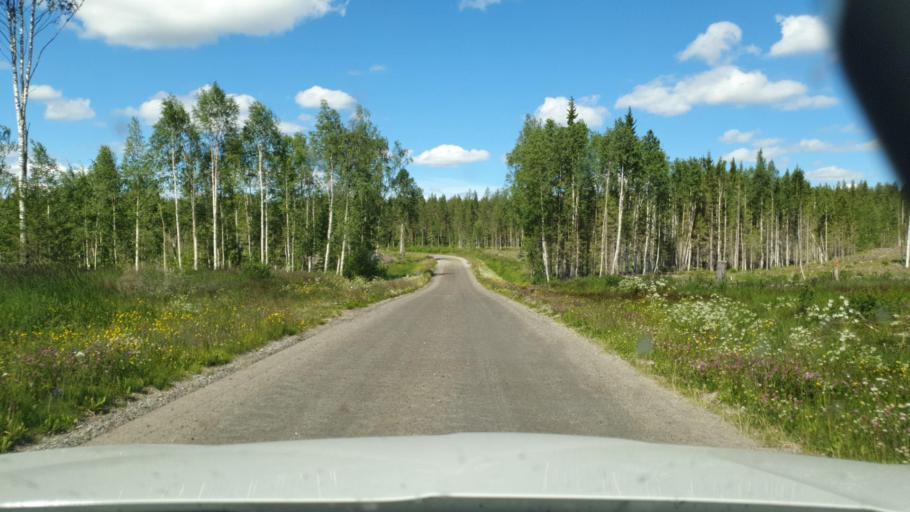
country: SE
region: Norrbotten
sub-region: Pitea Kommun
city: Roknas
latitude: 65.1589
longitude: 21.1562
